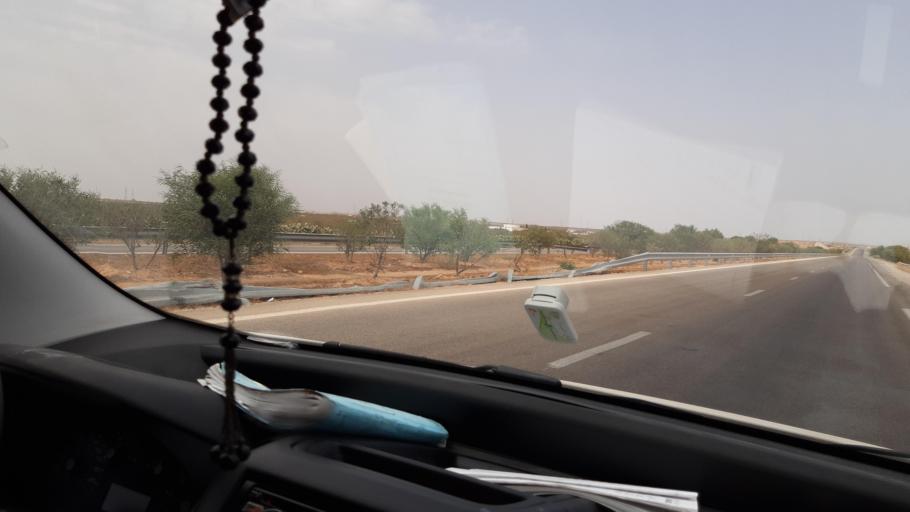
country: TN
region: Safaqis
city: Sfax
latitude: 34.8774
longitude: 10.6997
